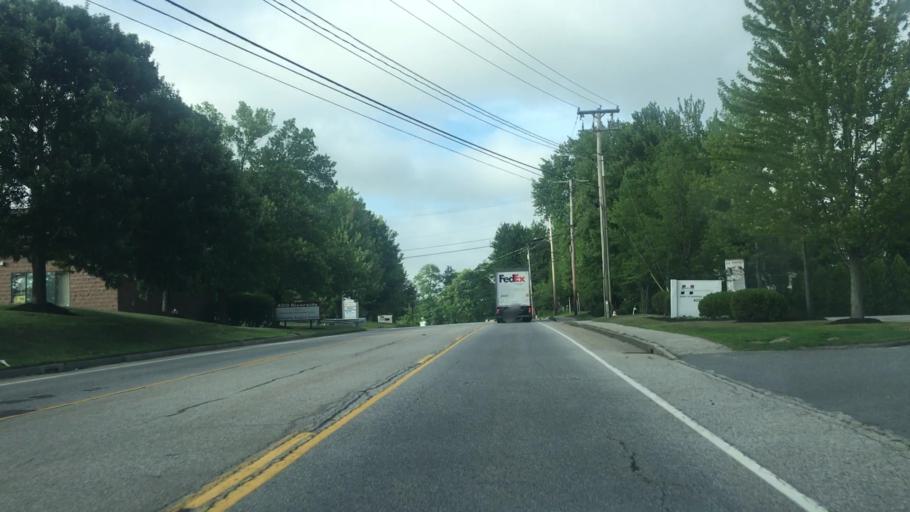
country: US
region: Maine
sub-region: Cumberland County
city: Westbrook
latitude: 43.6894
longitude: -70.3270
